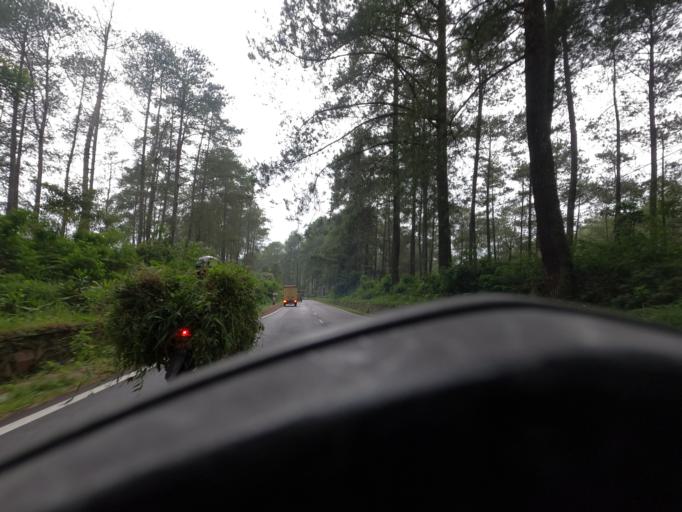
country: ID
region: West Java
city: Lembang
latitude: -6.7786
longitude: 107.6428
